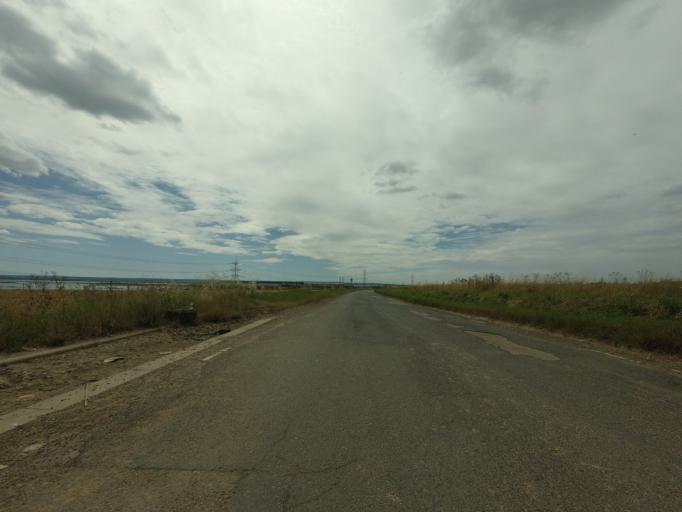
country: GB
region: England
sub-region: Medway
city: Stoke
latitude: 51.4419
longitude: 0.6201
